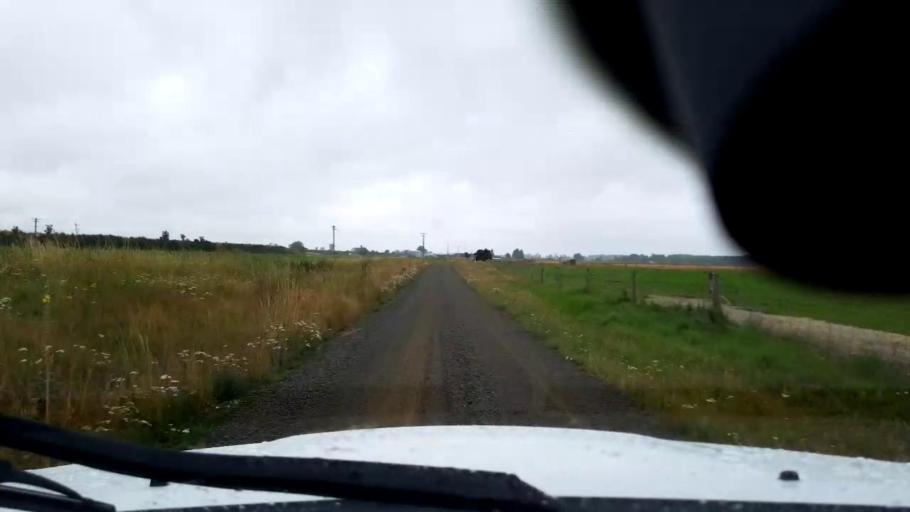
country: NZ
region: Canterbury
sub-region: Timaru District
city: Pleasant Point
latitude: -44.2535
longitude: 171.1981
